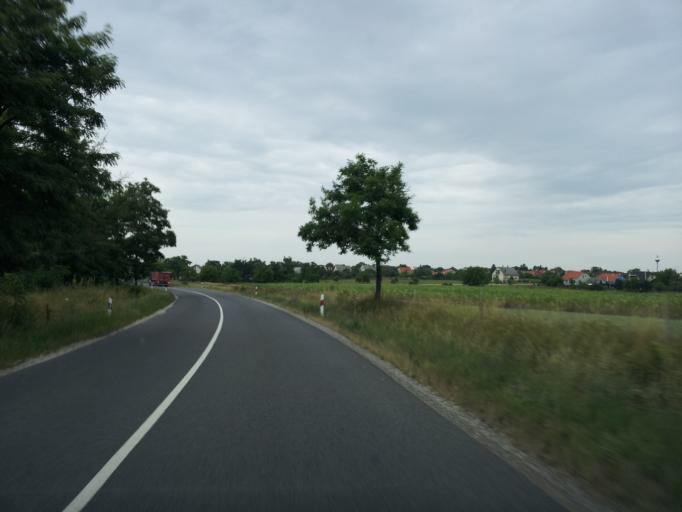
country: HU
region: Veszprem
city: Devecser
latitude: 47.0909
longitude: 17.4402
